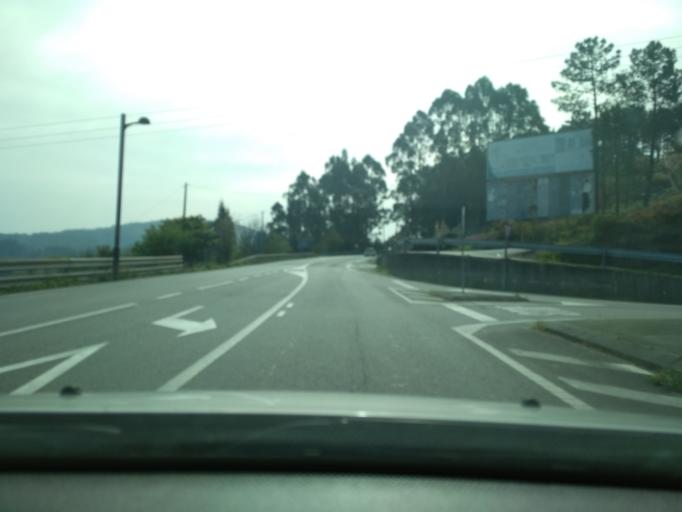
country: ES
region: Galicia
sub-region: Provincia de Pontevedra
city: Catoira
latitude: 42.6764
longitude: -8.7187
